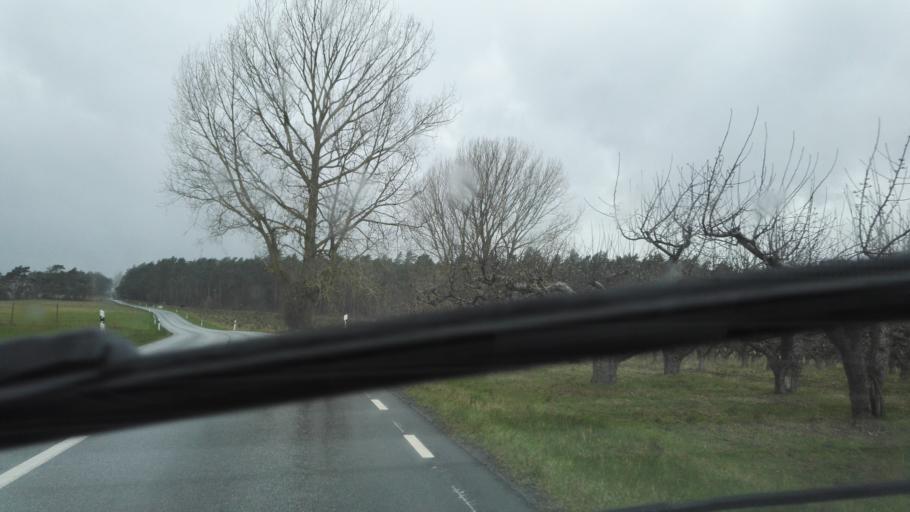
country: SE
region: Skane
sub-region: Simrishamns Kommun
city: Kivik
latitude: 55.7110
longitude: 14.1679
